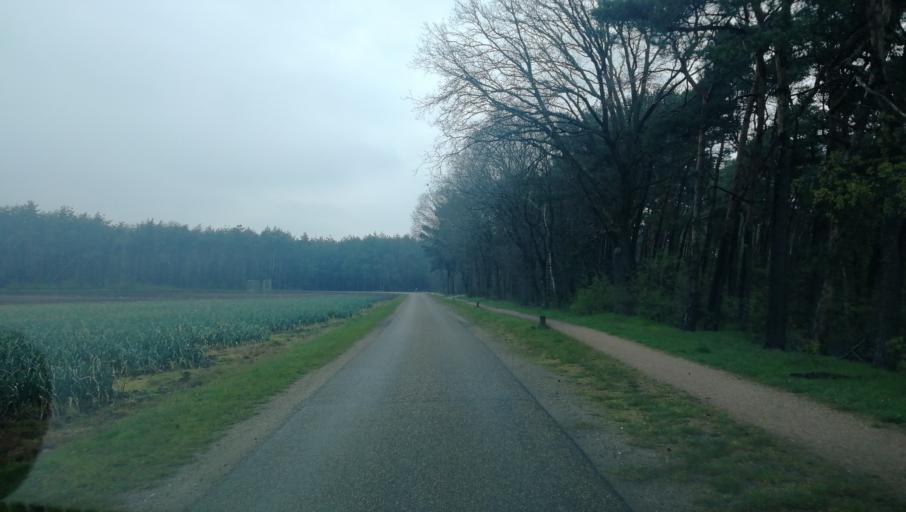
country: NL
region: Limburg
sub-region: Gemeente Beesel
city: Beesel
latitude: 51.3039
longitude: 5.9984
